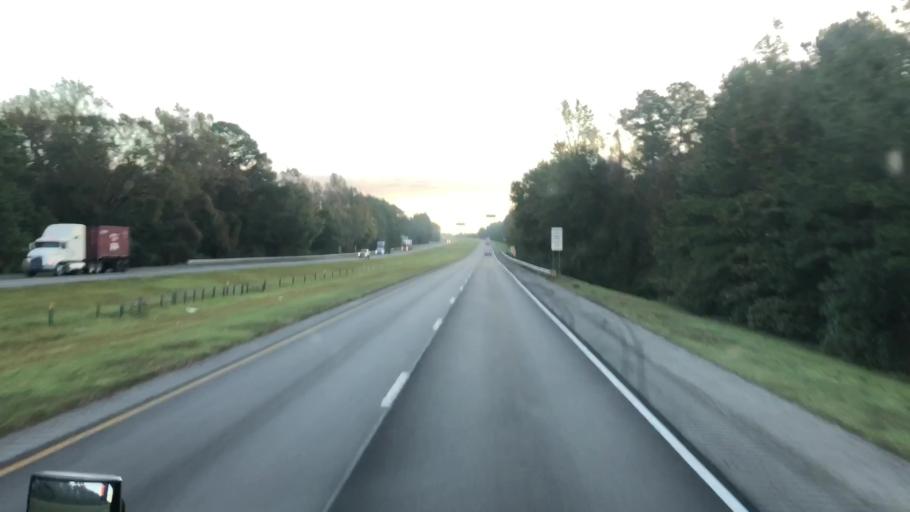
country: US
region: South Carolina
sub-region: Clarendon County
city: Manning
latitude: 33.5937
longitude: -80.3435
